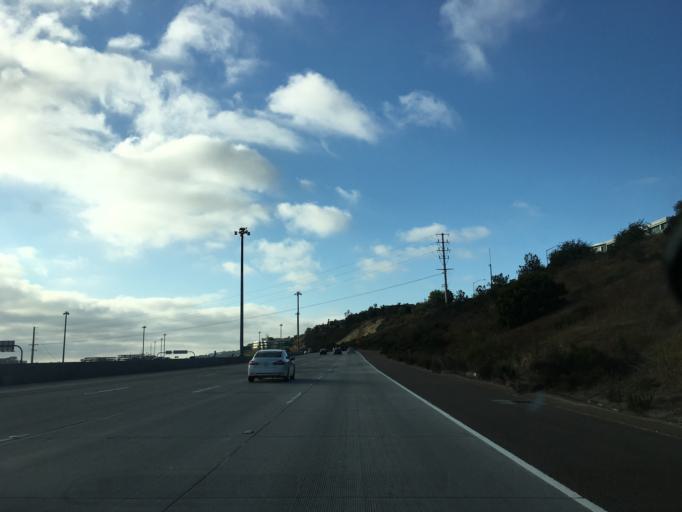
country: US
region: California
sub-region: San Diego County
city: Del Mar
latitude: 32.9126
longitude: -117.2284
